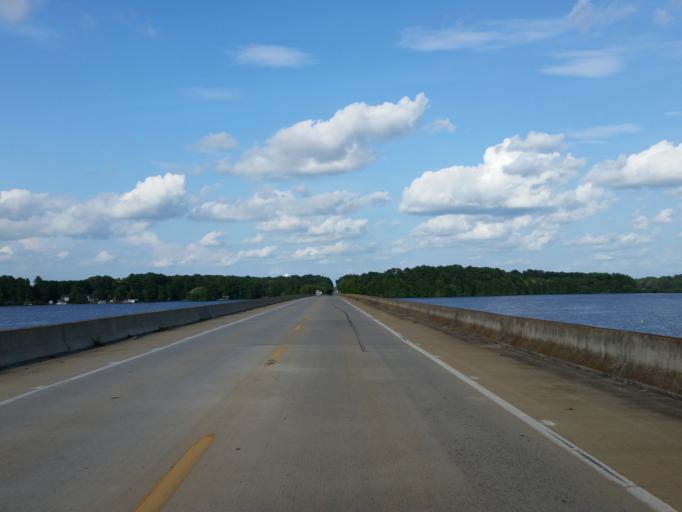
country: US
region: Georgia
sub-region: Crisp County
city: Cordele
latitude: 31.9647
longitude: -83.9343
